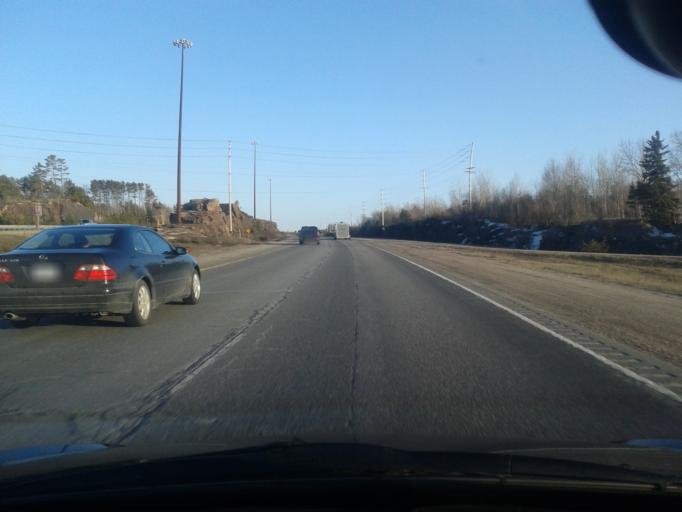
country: CA
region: Ontario
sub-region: Nipissing District
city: North Bay
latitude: 46.3040
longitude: -79.4316
